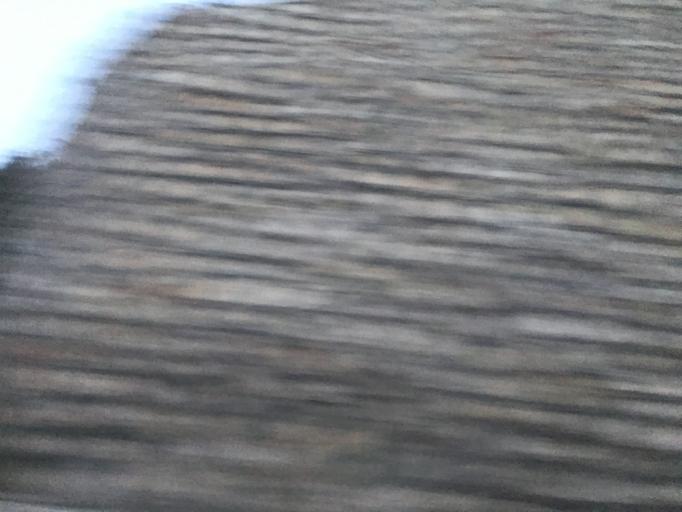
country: TR
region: Hatay
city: Karacay
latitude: 36.1514
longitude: 36.0915
